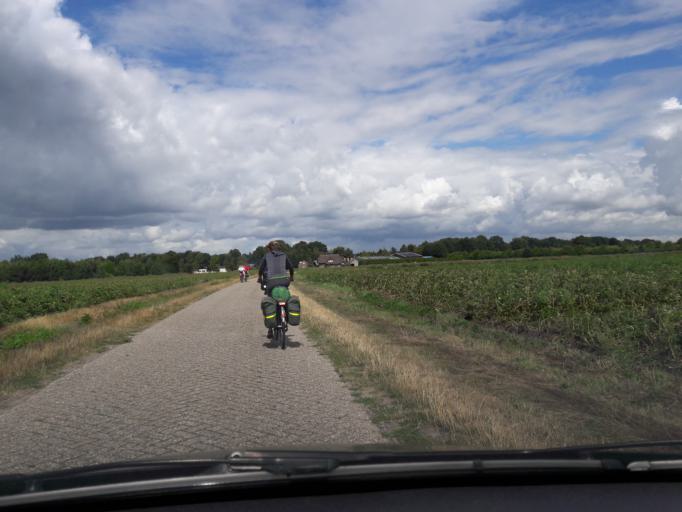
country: NL
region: Drenthe
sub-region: Gemeente Borger-Odoorn
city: Borger
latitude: 52.9470
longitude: 6.7975
